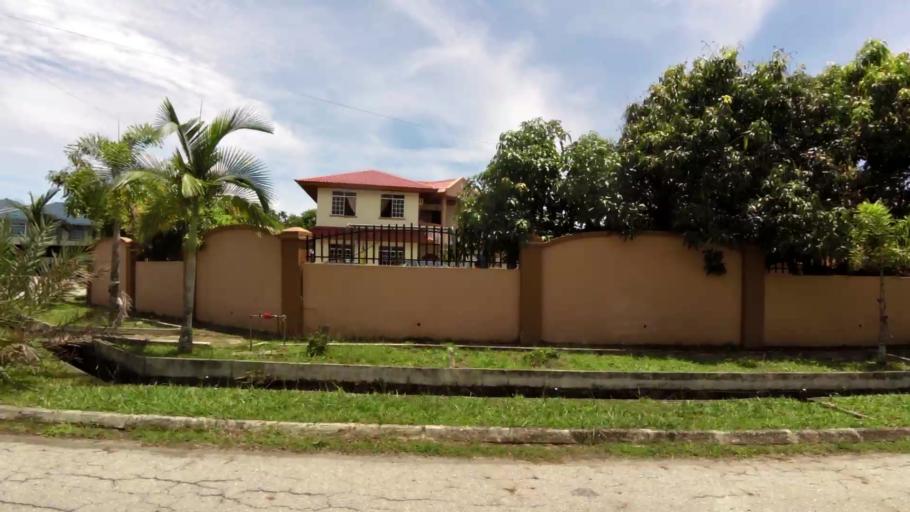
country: BN
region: Brunei and Muara
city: Bandar Seri Begawan
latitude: 4.9625
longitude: 114.9093
